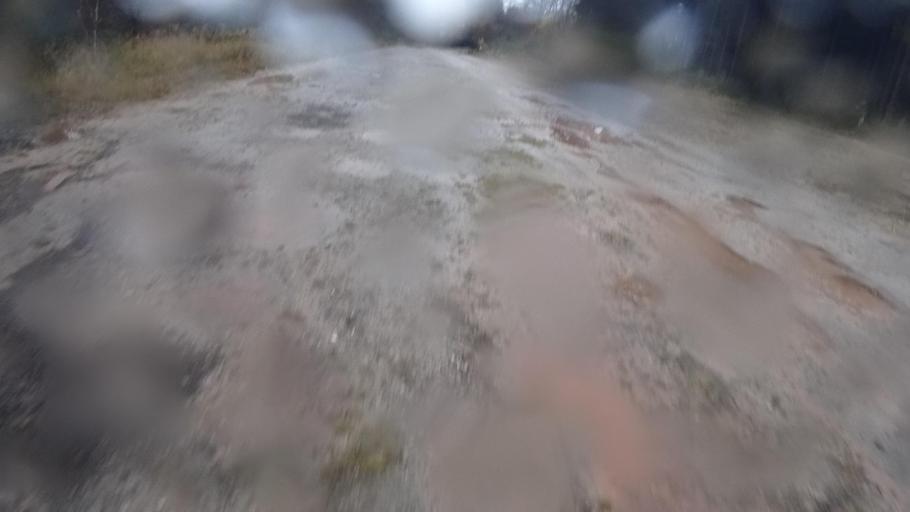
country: DE
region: Rheinland-Pfalz
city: Wiebelsheim
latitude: 50.0996
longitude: 7.6272
